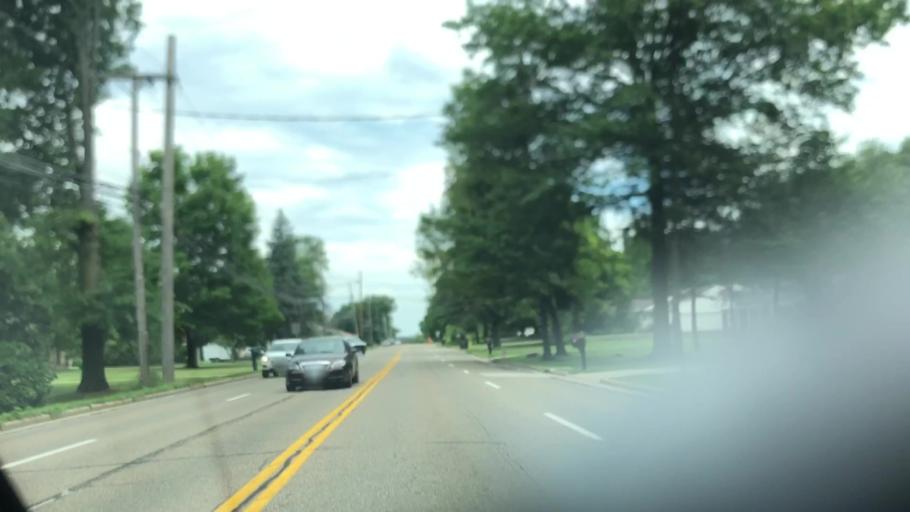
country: US
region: Ohio
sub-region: Summit County
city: Fairlawn
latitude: 41.1210
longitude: -81.6098
